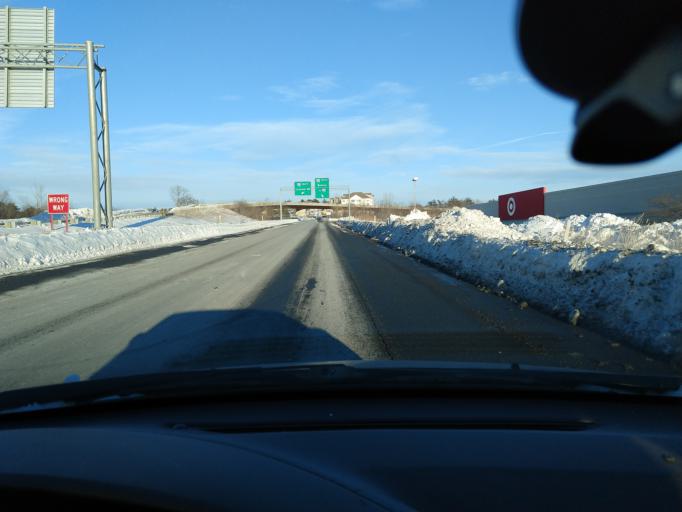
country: US
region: Massachusetts
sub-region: Middlesex County
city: Reading
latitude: 42.5189
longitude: -71.1365
